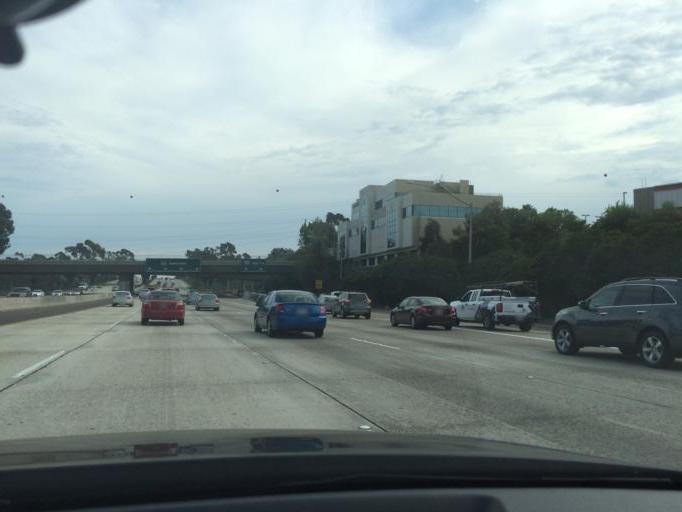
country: US
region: California
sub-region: San Diego County
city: San Diego
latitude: 32.8124
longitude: -117.1515
